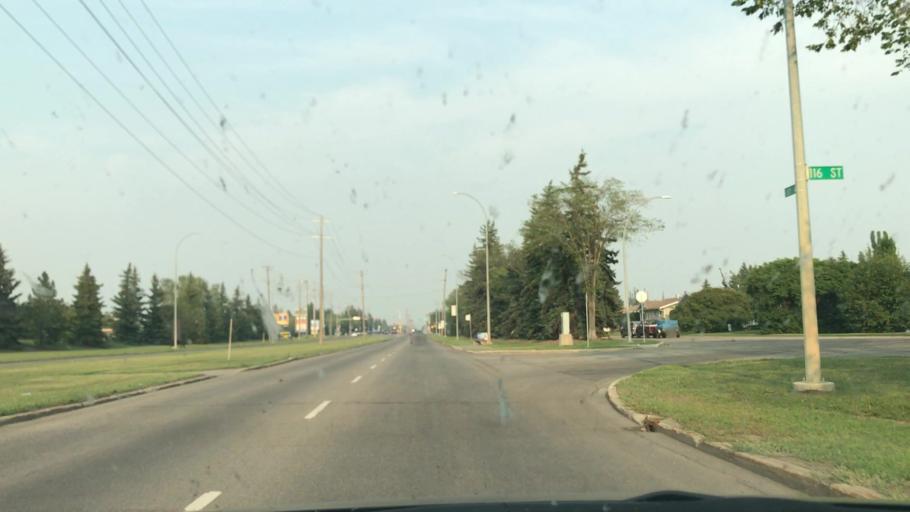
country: CA
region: Alberta
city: Edmonton
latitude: 53.5994
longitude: -113.5222
